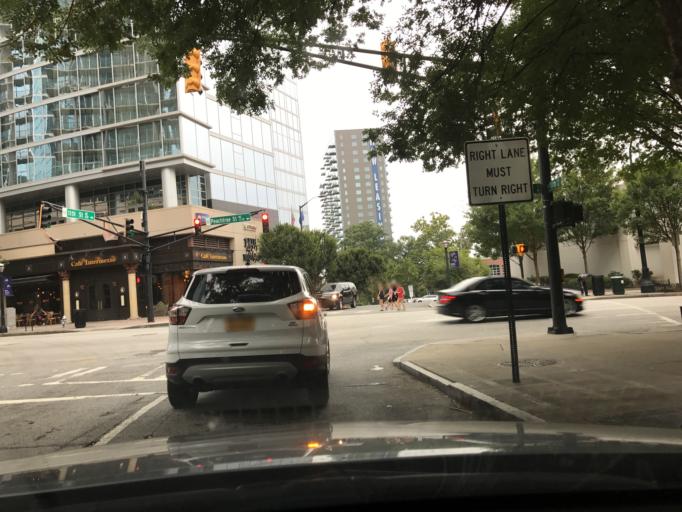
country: US
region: Georgia
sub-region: Fulton County
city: Atlanta
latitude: 33.7833
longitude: -84.3842
